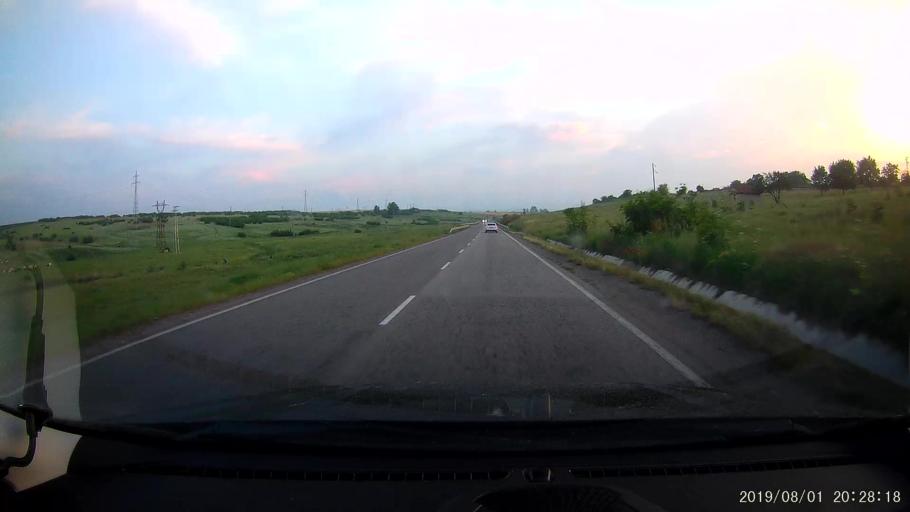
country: BG
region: Yambol
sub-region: Obshtina Elkhovo
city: Elkhovo
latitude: 42.1703
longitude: 26.5798
